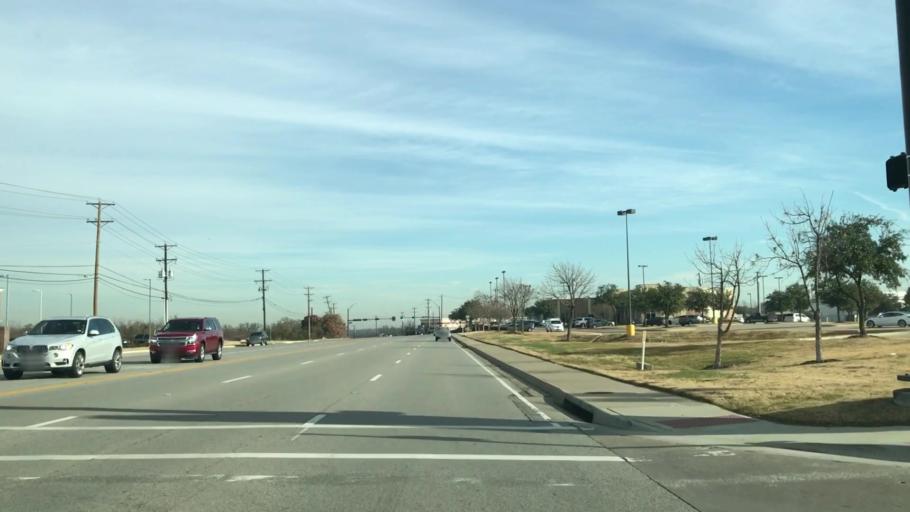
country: US
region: Texas
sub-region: Tarrant County
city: Colleyville
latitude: 32.9086
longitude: -97.1901
